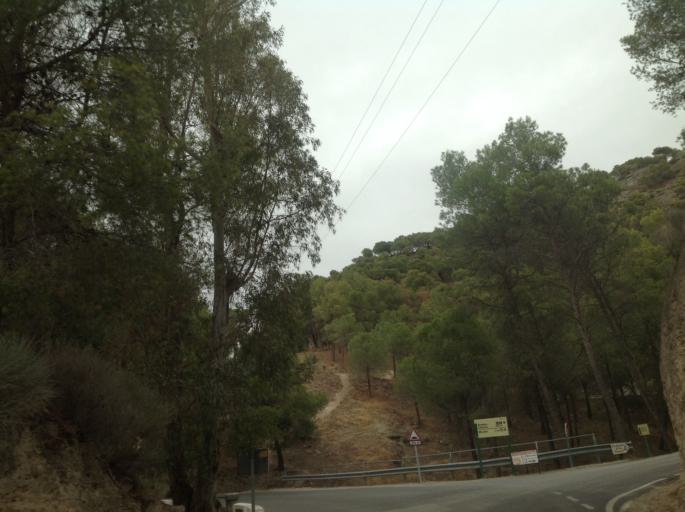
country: ES
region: Andalusia
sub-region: Provincia de Malaga
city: Ardales
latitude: 36.9274
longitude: -4.8013
